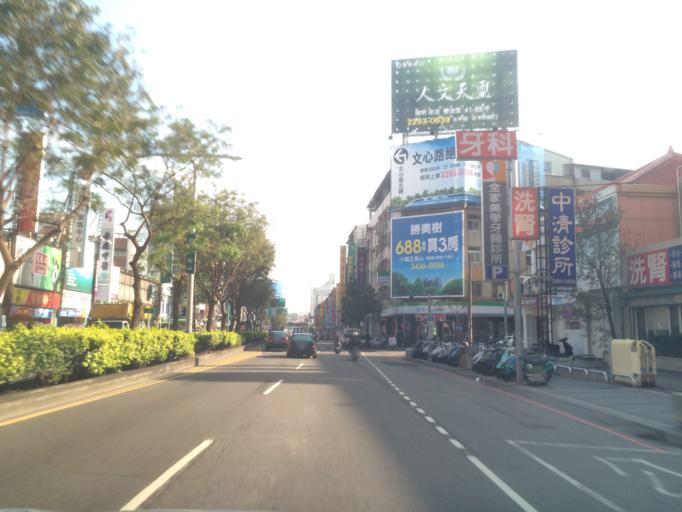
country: TW
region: Taiwan
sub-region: Taichung City
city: Taichung
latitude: 24.1807
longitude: 120.6667
